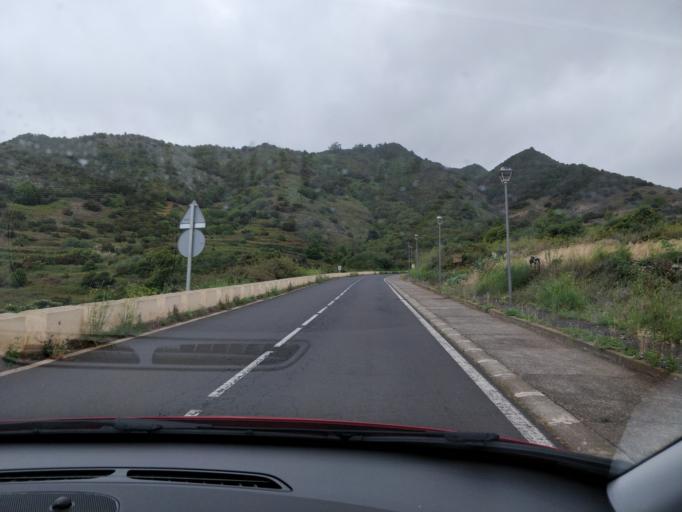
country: ES
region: Canary Islands
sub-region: Provincia de Santa Cruz de Tenerife
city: Tanque
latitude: 28.3290
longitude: -16.8444
